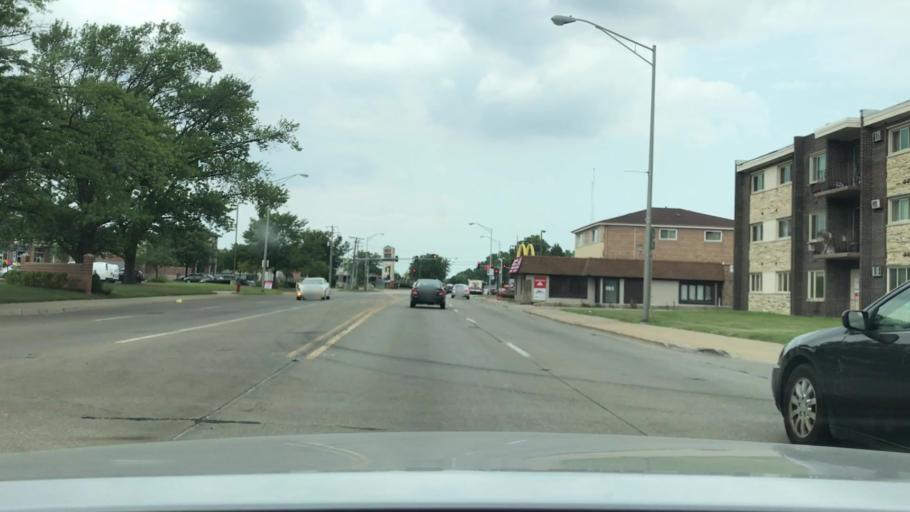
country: US
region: Illinois
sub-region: Cook County
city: Evergreen Park
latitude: 41.7334
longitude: -87.7022
